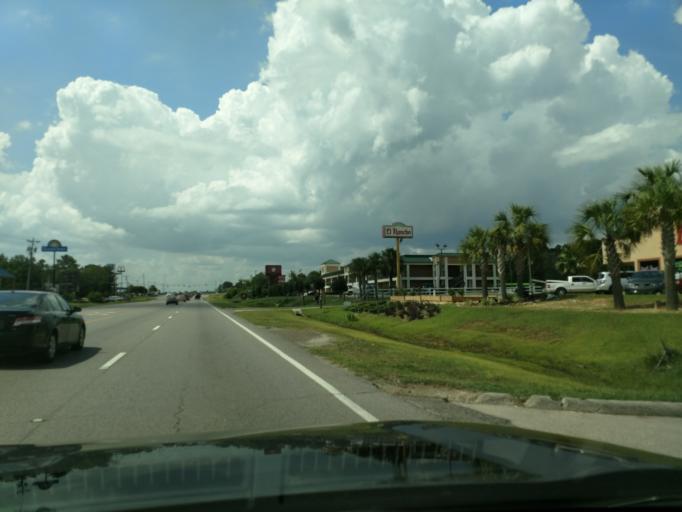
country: US
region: Mississippi
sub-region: Jackson County
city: Gulf Hills
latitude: 30.4468
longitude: -88.8401
